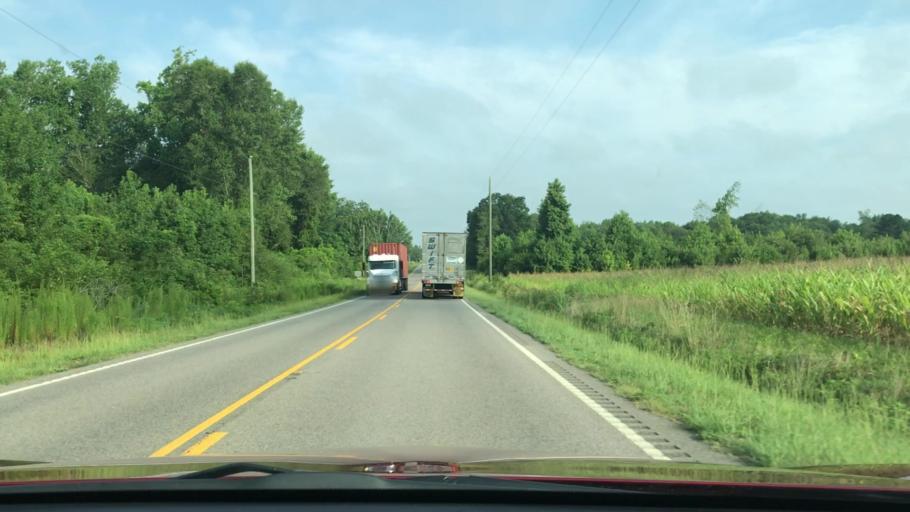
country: US
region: South Carolina
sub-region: Barnwell County
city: Williston
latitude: 33.6231
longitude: -81.2947
